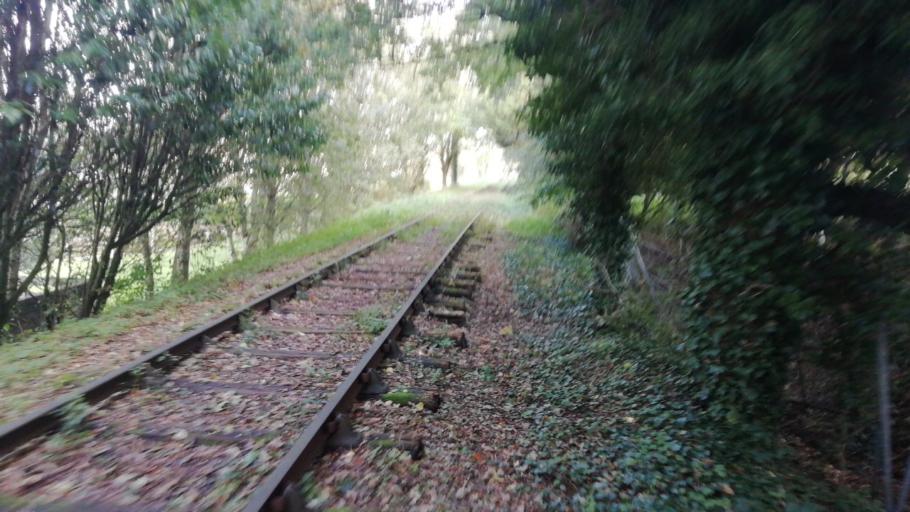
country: FR
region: Haute-Normandie
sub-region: Departement de la Seine-Maritime
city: Gonneville-la-Mallet
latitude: 49.6387
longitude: 0.2606
